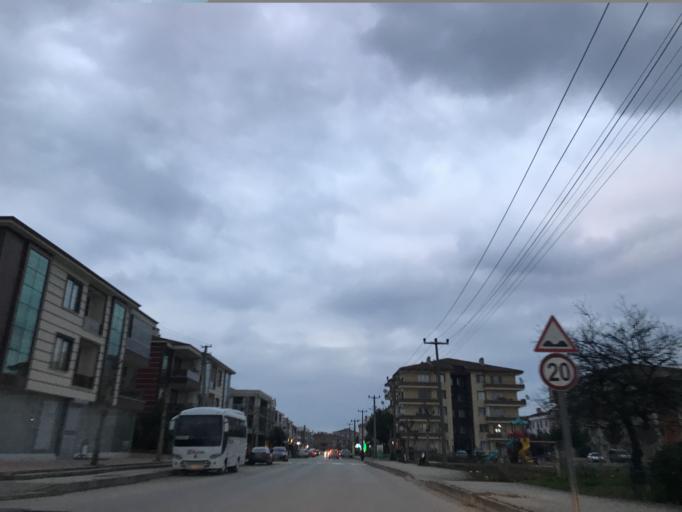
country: TR
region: Yalova
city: Yalova
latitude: 40.6442
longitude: 29.2597
